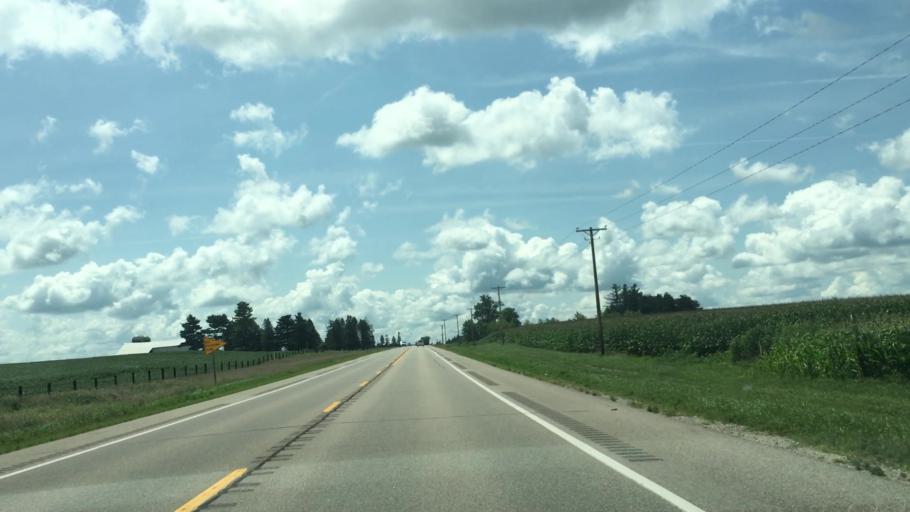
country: US
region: Iowa
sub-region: Johnson County
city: Solon
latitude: 41.8257
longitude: -91.4974
